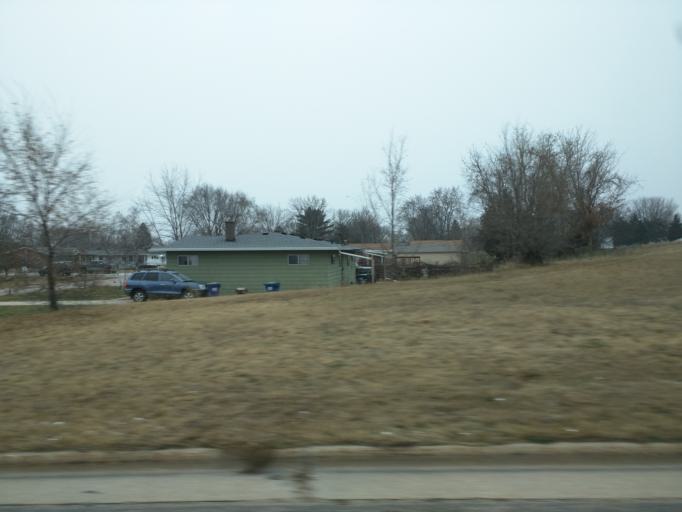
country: US
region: Wisconsin
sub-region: La Crosse County
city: French Island
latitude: 43.8657
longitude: -91.2615
